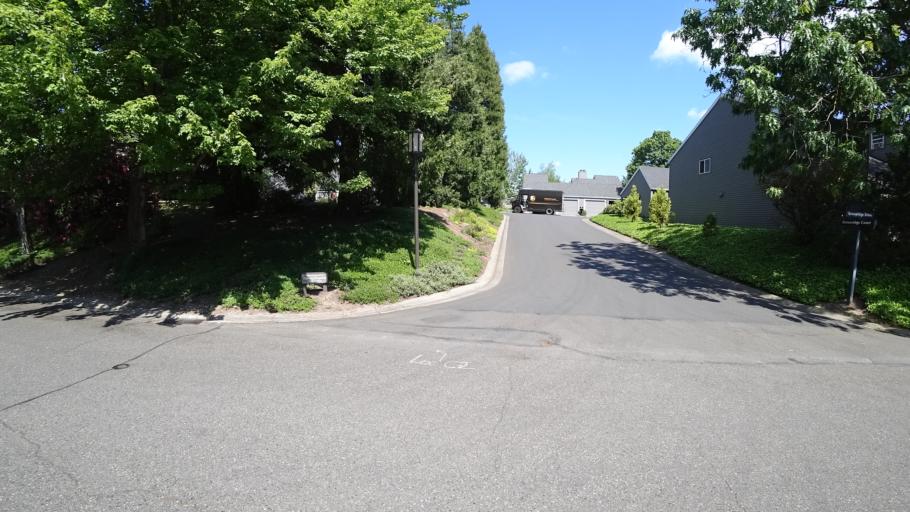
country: US
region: Oregon
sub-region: Clackamas County
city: Lake Oswego
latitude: 45.4313
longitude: -122.7063
